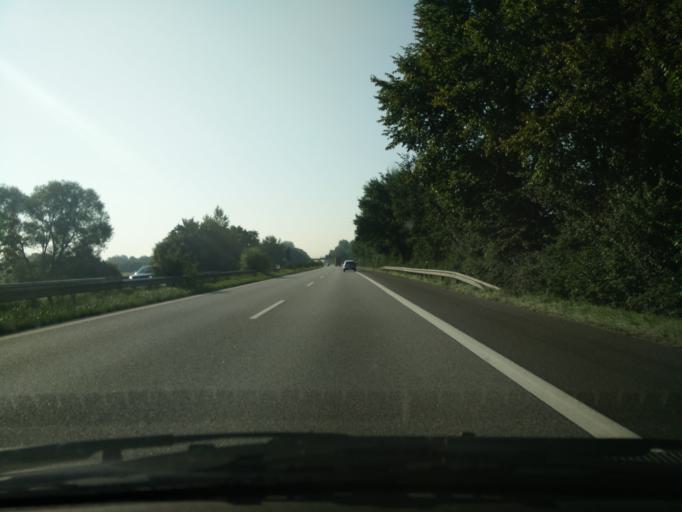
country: DE
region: Schleswig-Holstein
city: Kummerfeld
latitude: 53.6933
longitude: 9.7813
